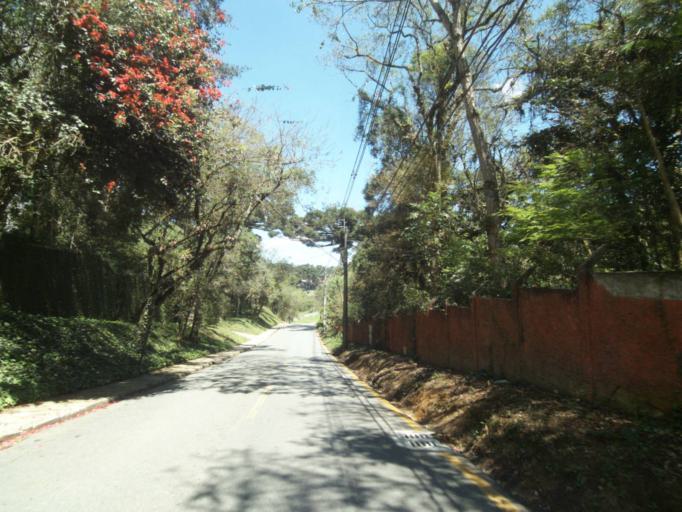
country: BR
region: Parana
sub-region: Curitiba
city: Curitiba
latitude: -25.3780
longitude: -49.2656
